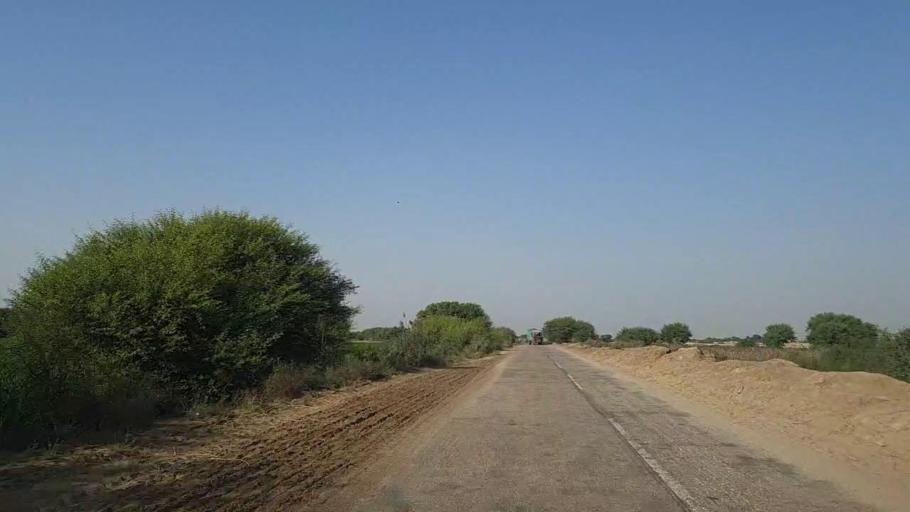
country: PK
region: Sindh
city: Mirpur Batoro
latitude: 24.5756
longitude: 68.3946
